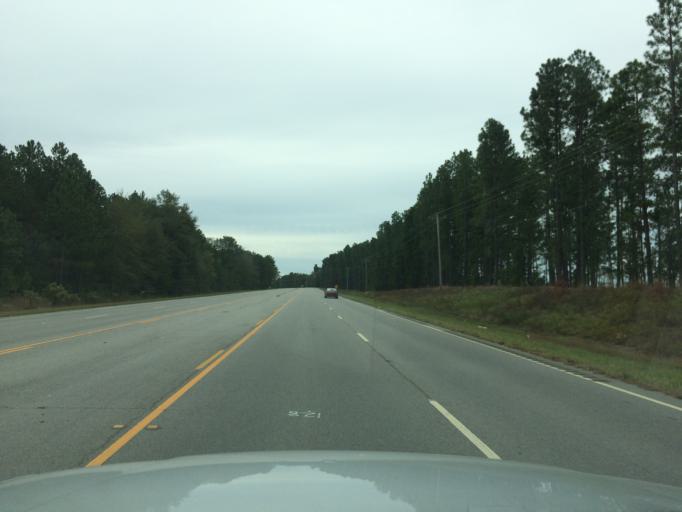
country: US
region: South Carolina
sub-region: Aiken County
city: Aiken
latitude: 33.6310
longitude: -81.6785
